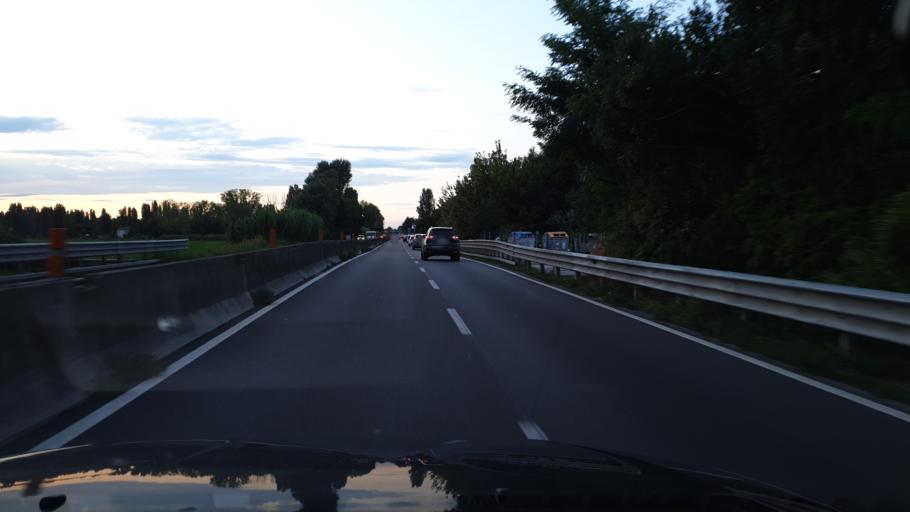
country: IT
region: Emilia-Romagna
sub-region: Provincia di Ravenna
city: Ravenna
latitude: 44.4041
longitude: 12.1774
